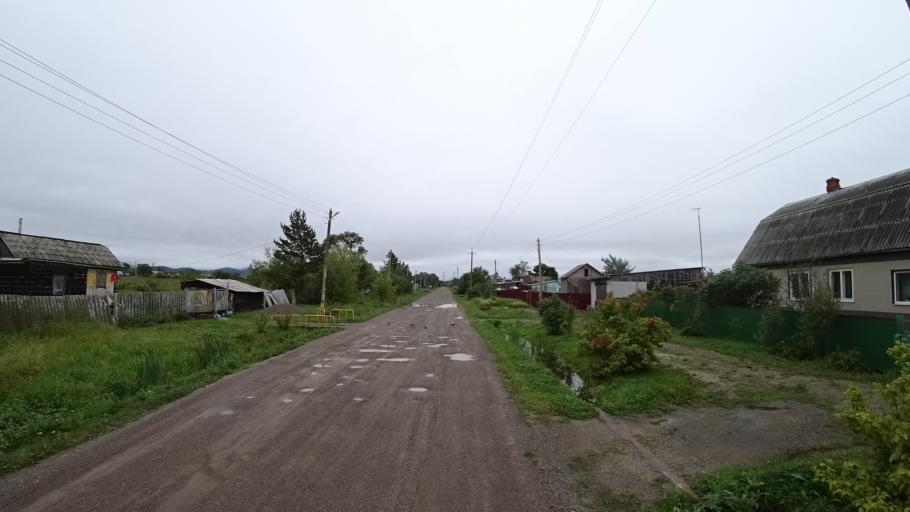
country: RU
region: Primorskiy
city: Monastyrishche
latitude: 44.1981
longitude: 132.4564
